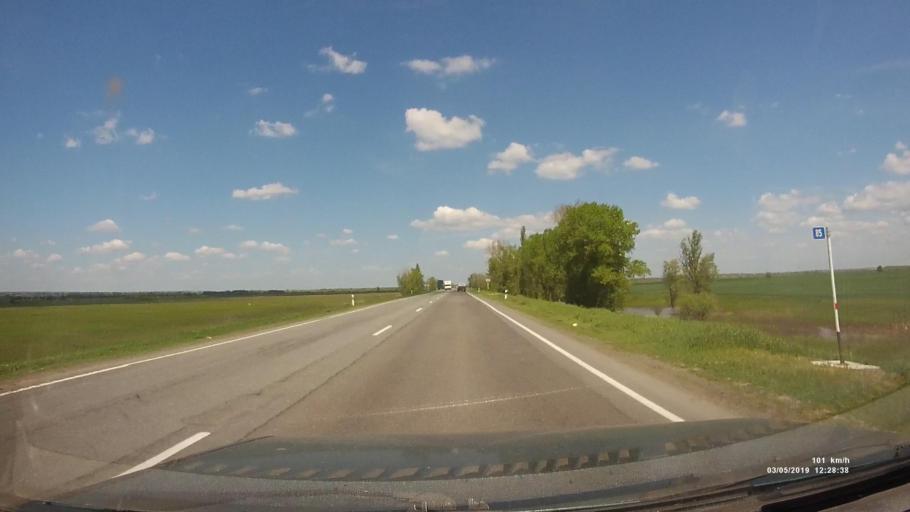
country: RU
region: Rostov
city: Semikarakorsk
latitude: 47.4762
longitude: 40.7302
